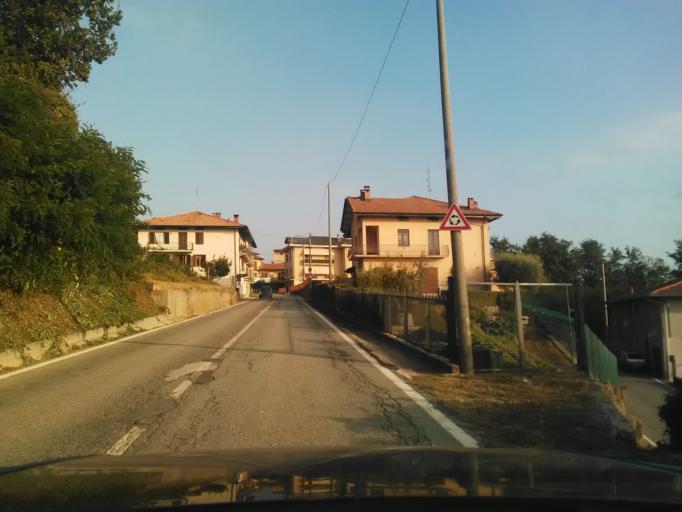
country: IT
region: Piedmont
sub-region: Provincia di Biella
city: Tollegno
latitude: 45.5849
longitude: 8.0668
